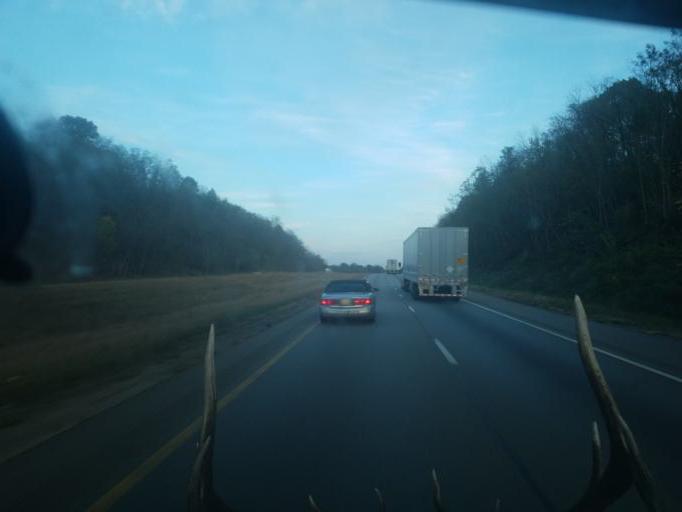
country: US
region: Ohio
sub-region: Muskingum County
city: New Concord
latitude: 39.9781
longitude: -81.7777
